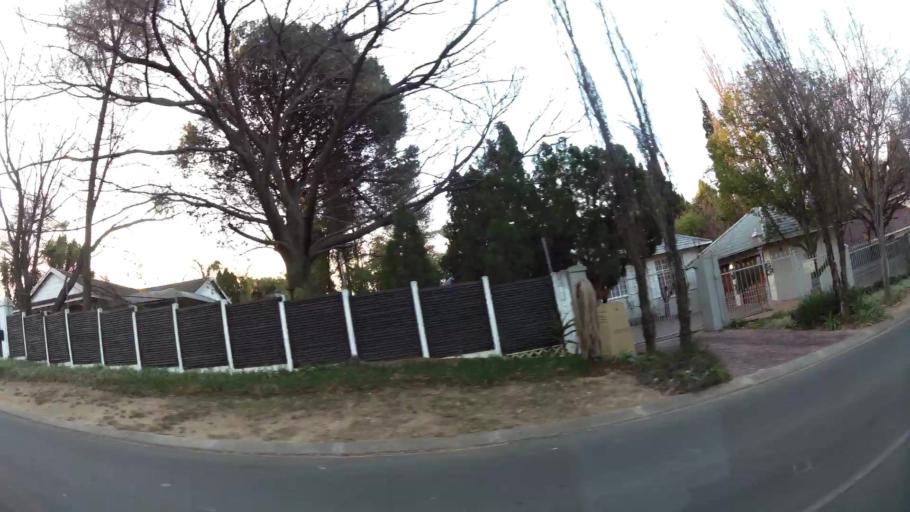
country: ZA
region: Gauteng
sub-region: City of Johannesburg Metropolitan Municipality
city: Diepsloot
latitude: -26.0173
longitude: 28.0364
